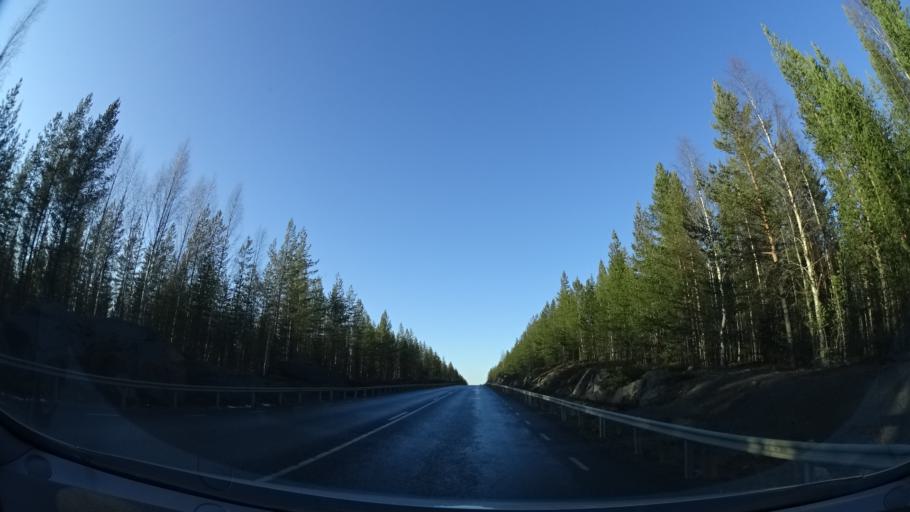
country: SE
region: Vaesterbotten
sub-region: Skelleftea Kommun
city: Langsele
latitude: 64.8873
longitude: 20.1899
